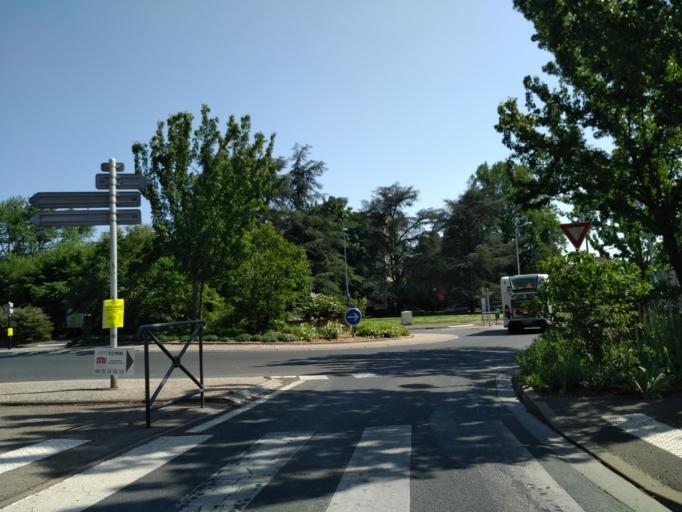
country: FR
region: Rhone-Alpes
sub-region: Departement du Rhone
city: Caluire-et-Cuire
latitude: 45.7998
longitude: 4.8197
